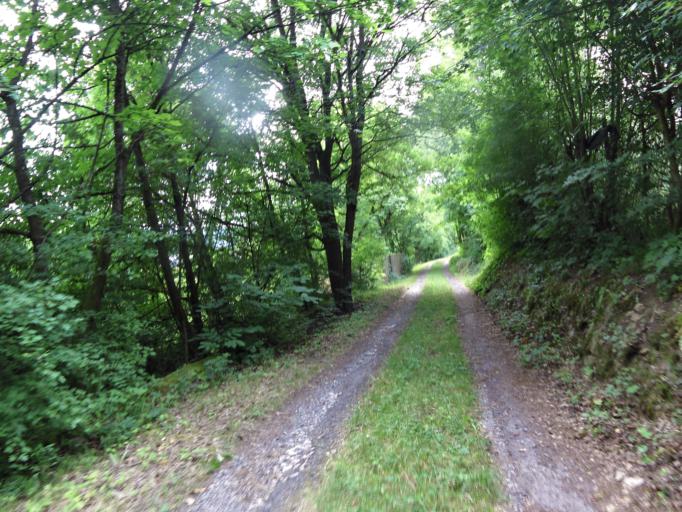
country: DE
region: Bavaria
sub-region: Regierungsbezirk Unterfranken
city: Wuerzburg
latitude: 49.7679
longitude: 9.9283
